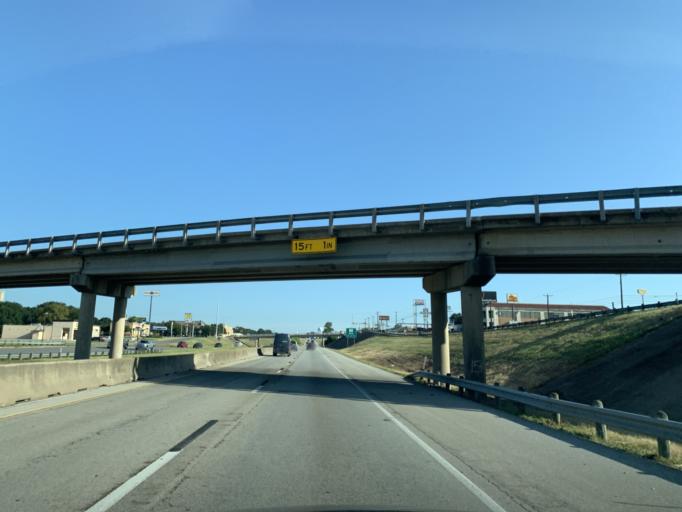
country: US
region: Texas
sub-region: Tarrant County
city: Azle
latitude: 32.8895
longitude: -97.5395
